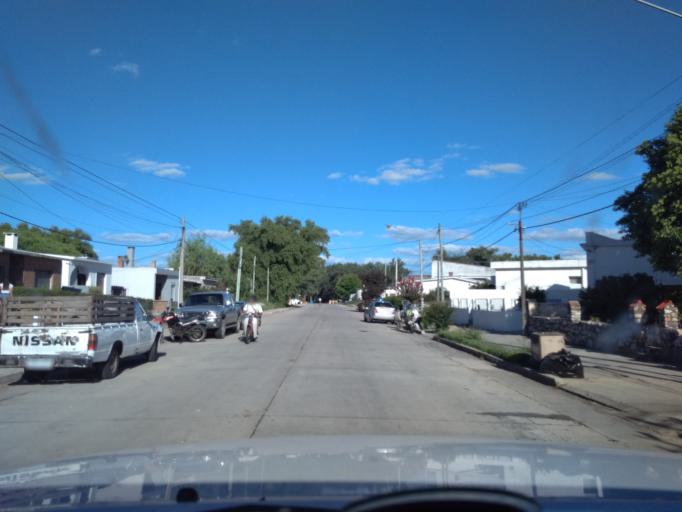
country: UY
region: Florida
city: Florida
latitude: -34.0923
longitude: -56.2110
